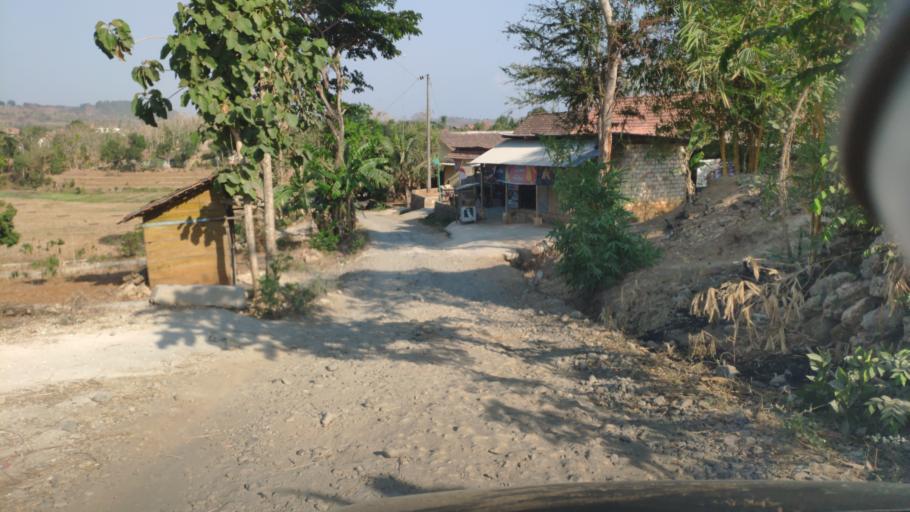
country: ID
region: Central Java
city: Ketringan
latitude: -6.9558
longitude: 111.5550
